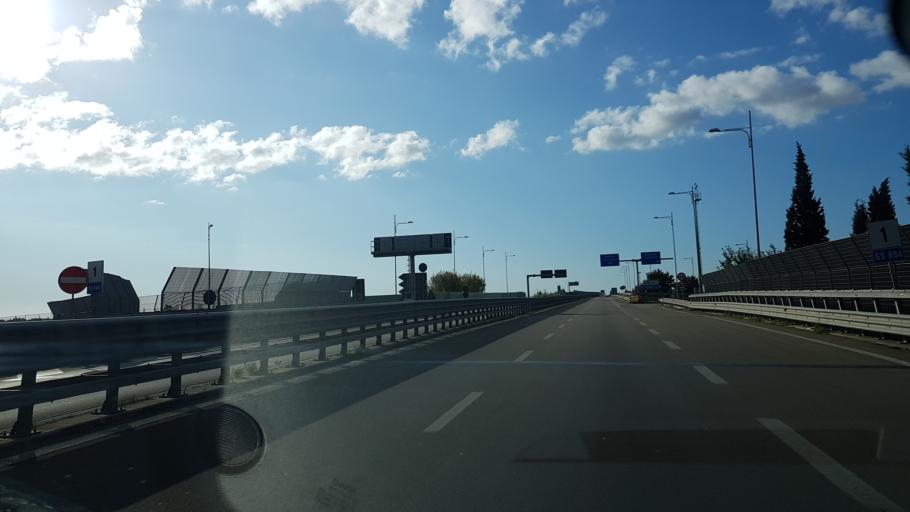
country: IT
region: Apulia
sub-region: Provincia di Lecce
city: Giorgilorio
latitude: 40.3650
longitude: 18.1433
